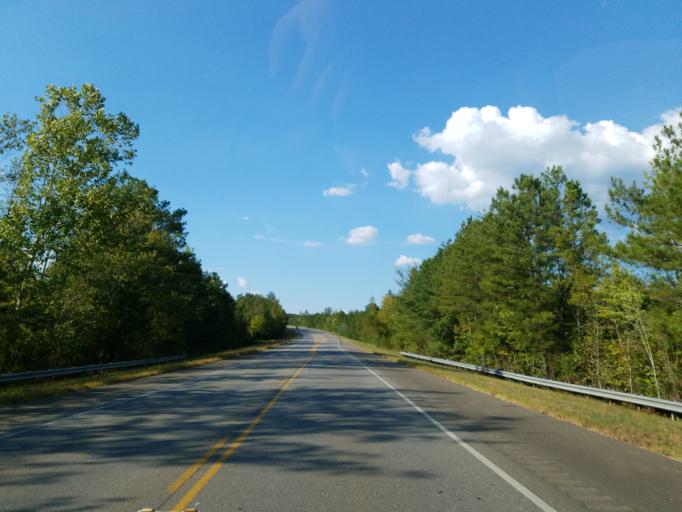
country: US
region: Georgia
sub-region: Murray County
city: Chatsworth
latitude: 34.6641
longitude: -84.7211
